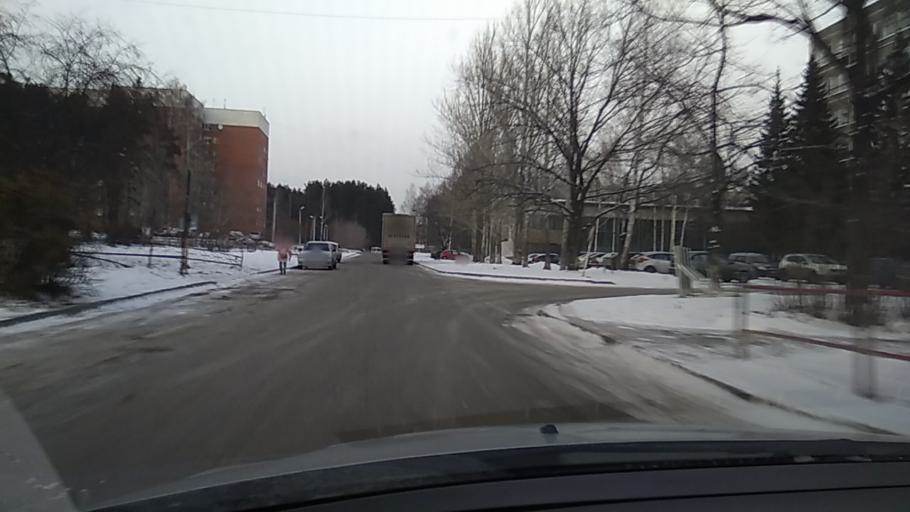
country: RU
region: Sverdlovsk
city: Istok
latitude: 56.7613
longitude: 60.7166
